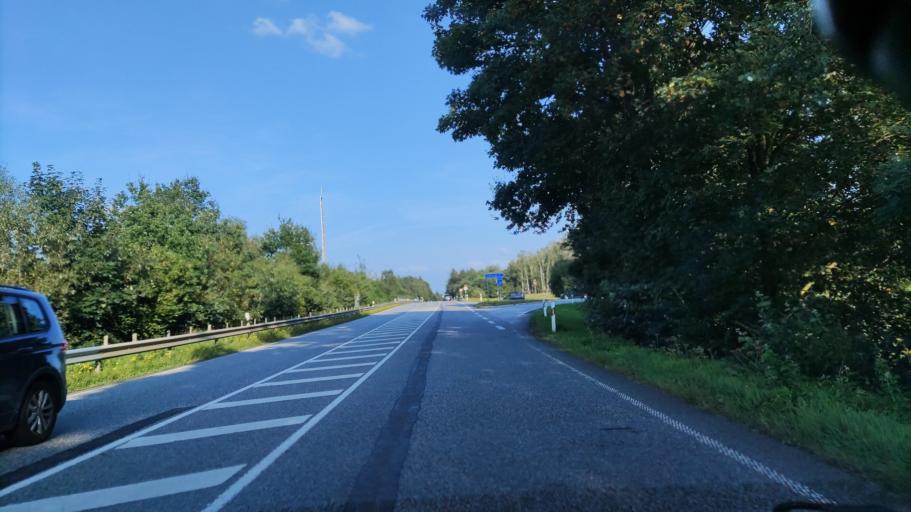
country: DE
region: Schleswig-Holstein
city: Bimohlen
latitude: 53.9044
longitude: 9.9337
